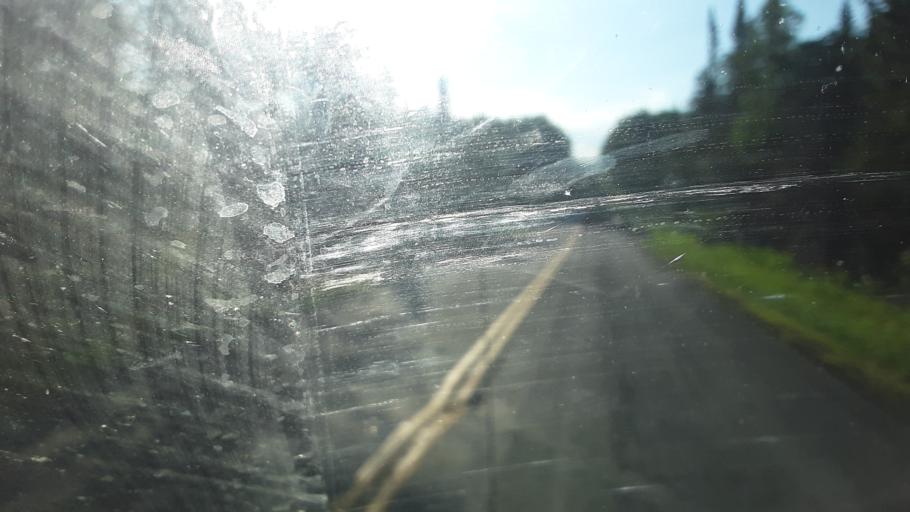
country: US
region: Maine
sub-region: Penobscot County
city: Patten
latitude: 46.2022
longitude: -68.2869
